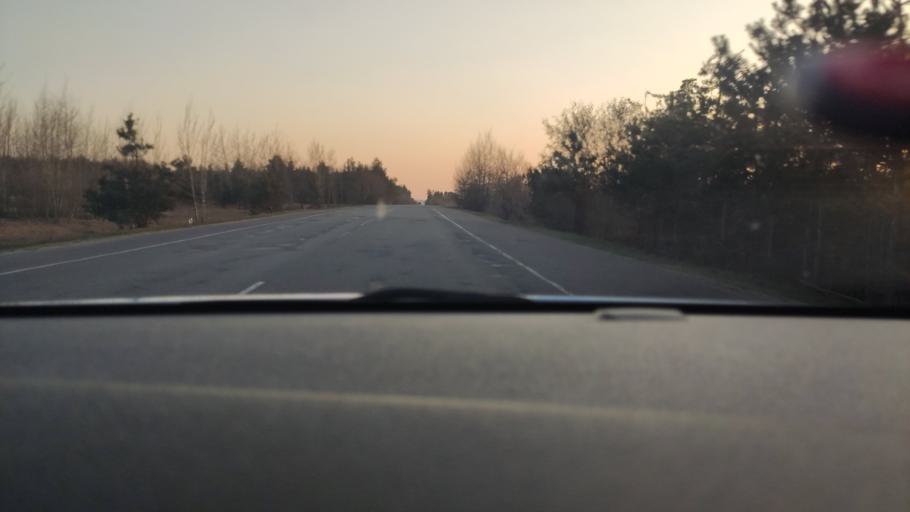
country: RU
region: Voronezj
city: Kolodeznyy
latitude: 51.3704
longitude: 39.2048
